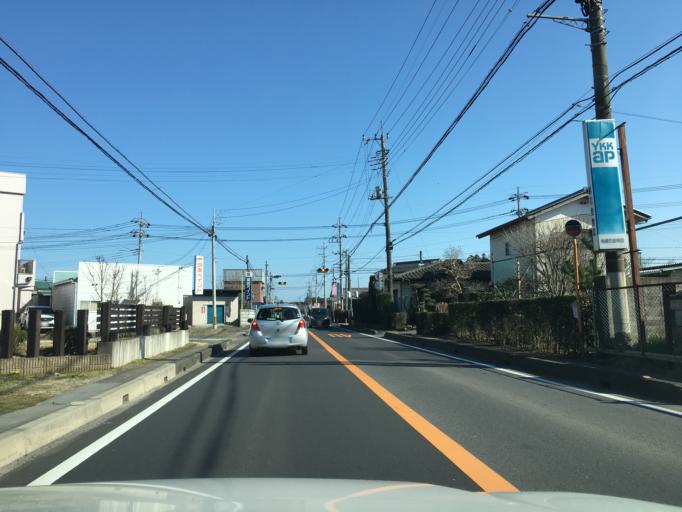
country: JP
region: Ibaraki
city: Omiya
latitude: 36.4769
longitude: 140.3815
